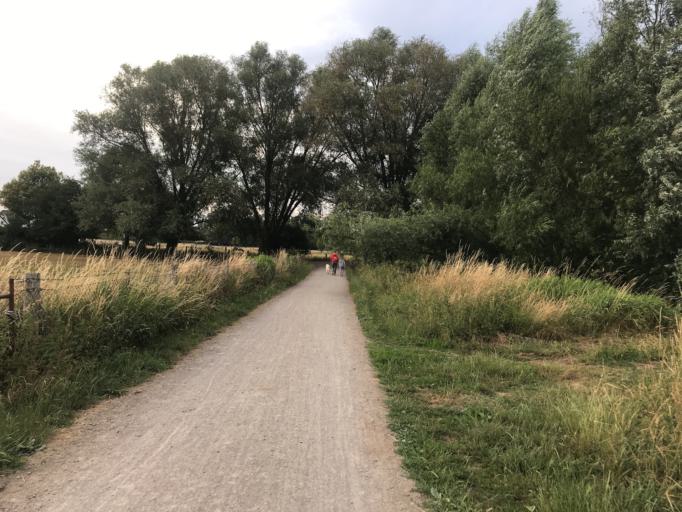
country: DE
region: Lower Saxony
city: Isernhagen Farster Bauerschaft
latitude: 52.4210
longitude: 9.8169
